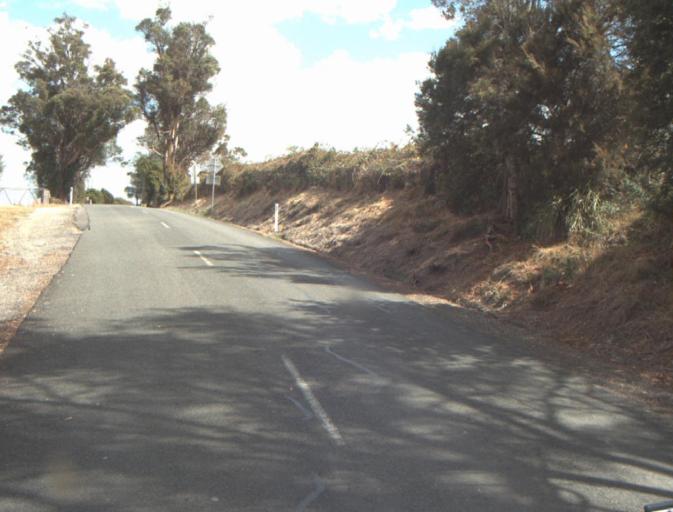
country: AU
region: Tasmania
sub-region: Launceston
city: Mayfield
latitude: -41.3107
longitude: 147.0455
